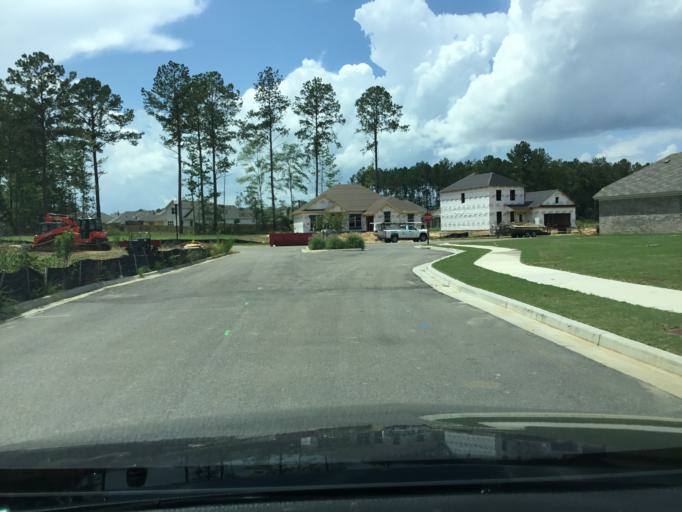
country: US
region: Alabama
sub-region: Montgomery County
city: Pike Road
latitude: 32.3346
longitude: -86.0709
